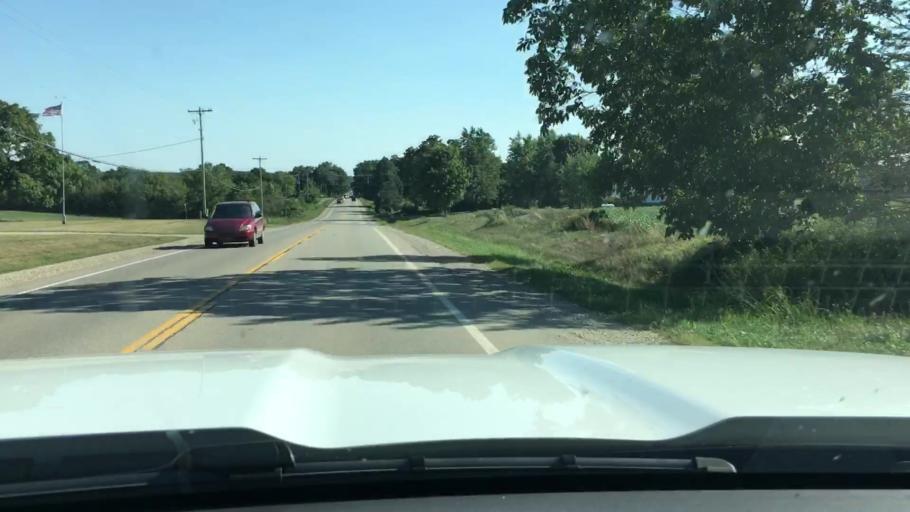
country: US
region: Michigan
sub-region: Ottawa County
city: Coopersville
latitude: 43.0251
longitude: -85.9563
